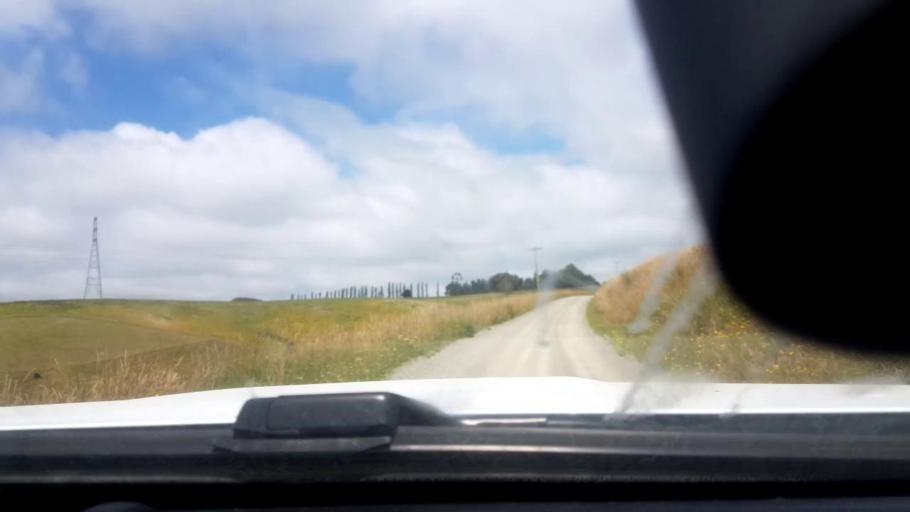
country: NZ
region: Canterbury
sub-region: Timaru District
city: Pleasant Point
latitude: -44.1506
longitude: 171.1533
